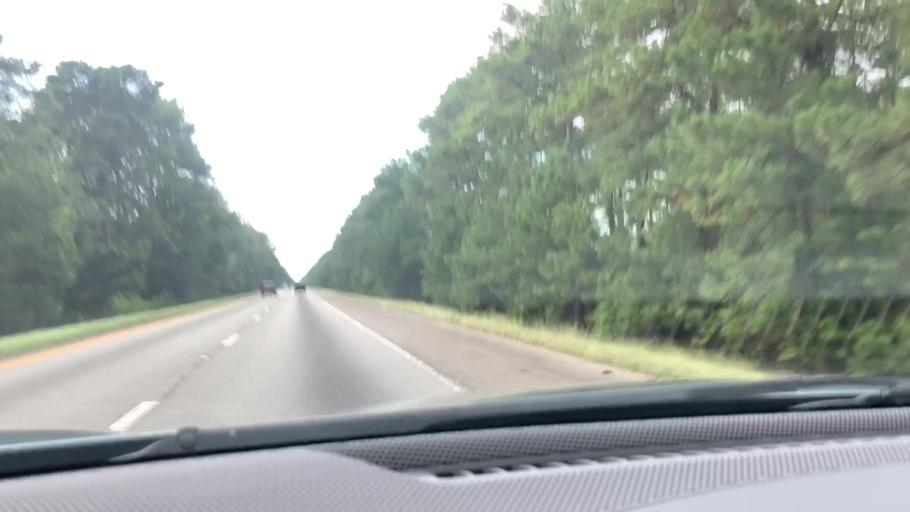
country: US
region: South Carolina
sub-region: Dorchester County
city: Saint George
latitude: 33.3319
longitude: -80.5615
